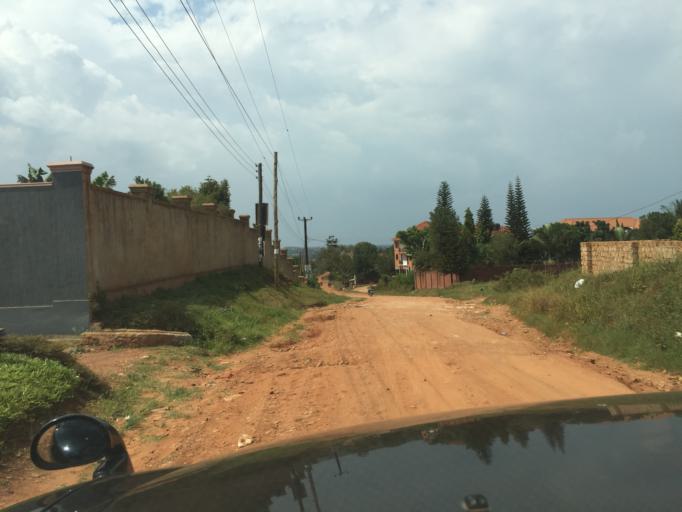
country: UG
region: Central Region
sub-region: Wakiso District
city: Kireka
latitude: 0.4070
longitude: 32.6198
